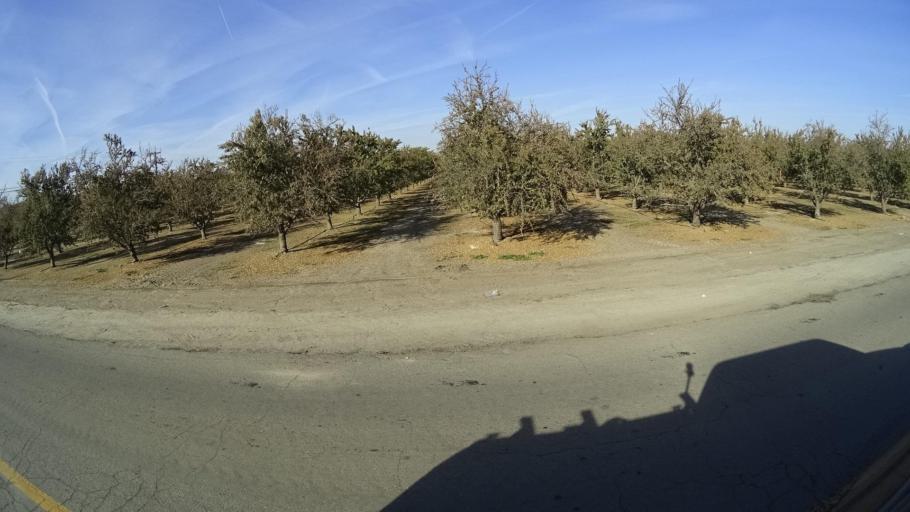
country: US
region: California
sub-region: Kern County
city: McFarland
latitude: 35.7033
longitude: -119.2403
